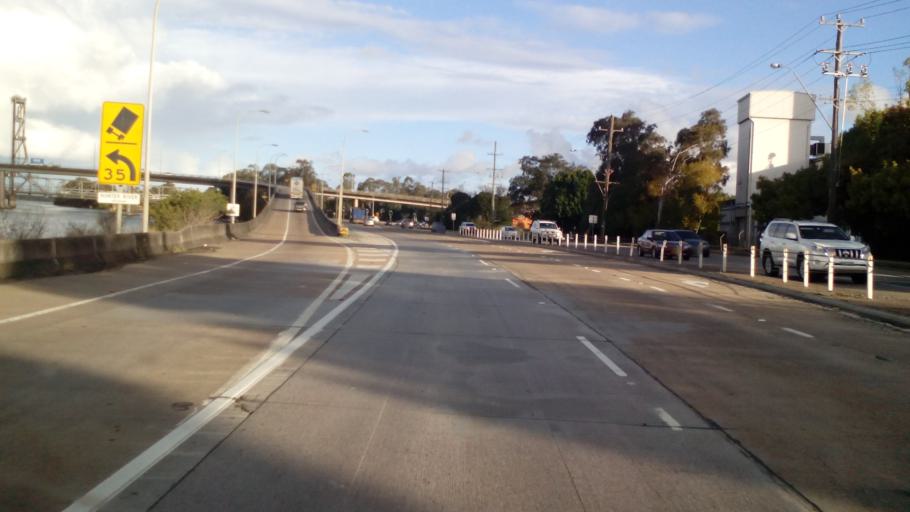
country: AU
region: New South Wales
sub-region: Newcastle
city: Beresfield
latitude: -32.8215
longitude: 151.6823
